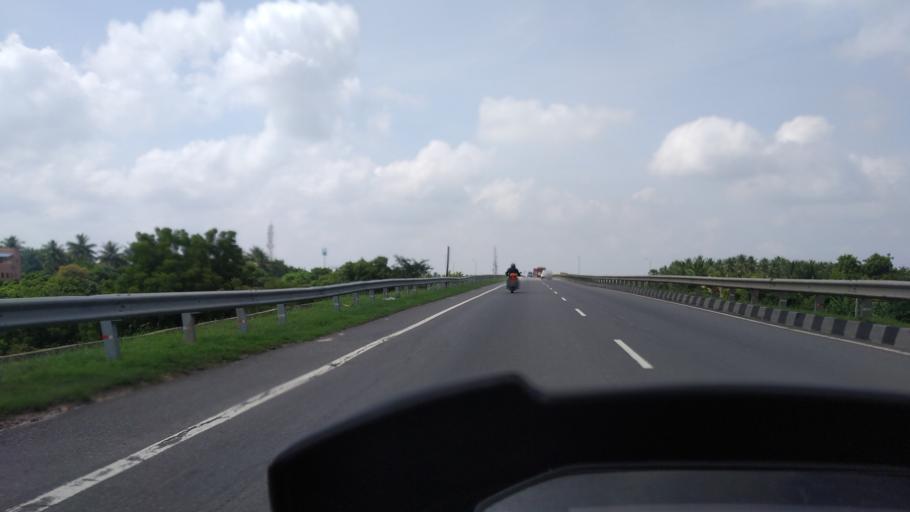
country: IN
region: Tamil Nadu
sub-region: Erode
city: Perundurai
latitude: 11.2609
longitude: 77.5516
